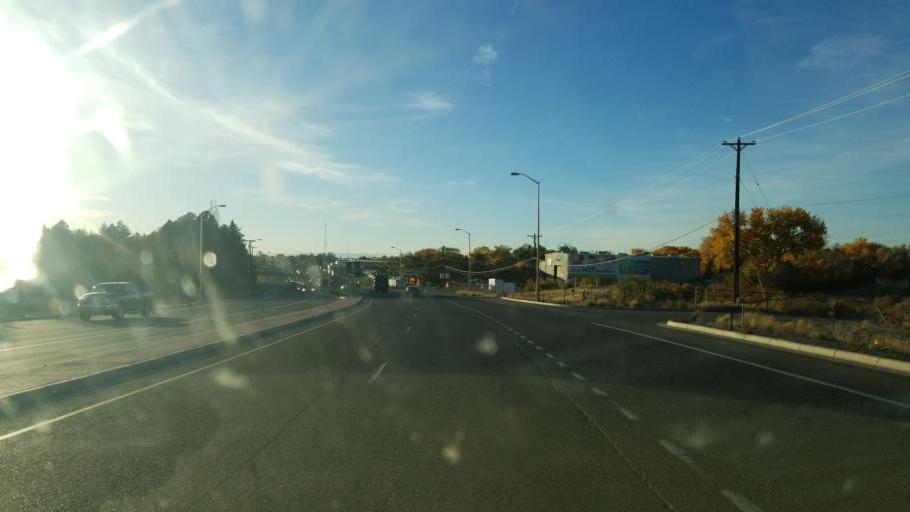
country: US
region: New Mexico
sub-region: San Juan County
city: Farmington
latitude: 36.7190
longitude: -108.1585
